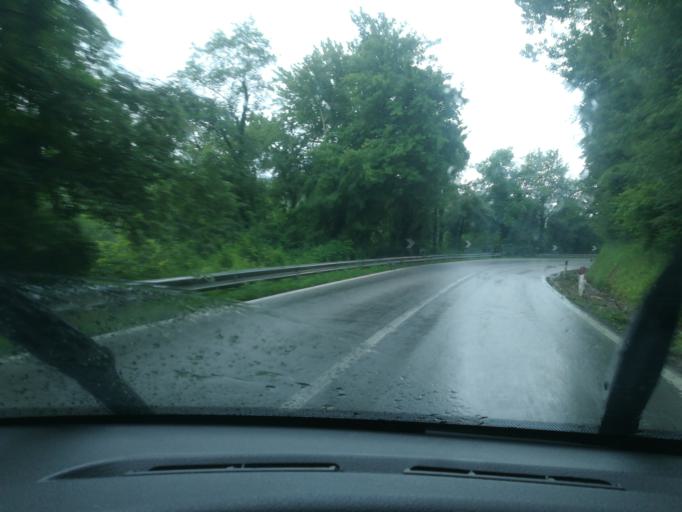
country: IT
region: The Marches
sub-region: Provincia di Macerata
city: Sarnano
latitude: 43.0582
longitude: 13.2757
